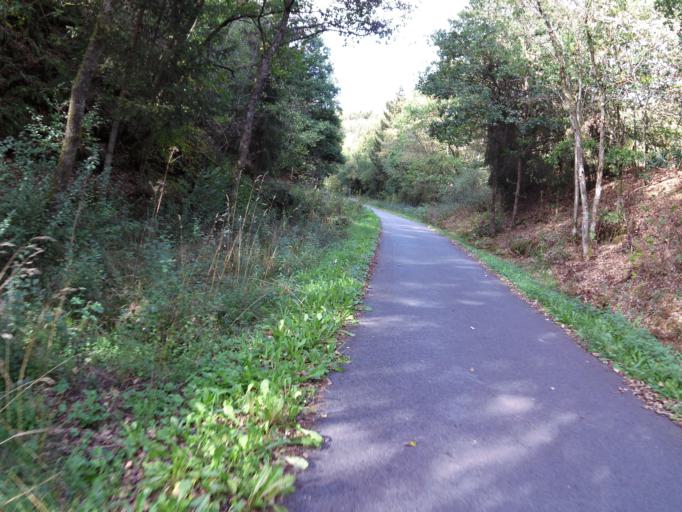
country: BE
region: Wallonia
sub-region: Province de Liege
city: Saint-Vith
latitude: 50.2382
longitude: 6.1564
